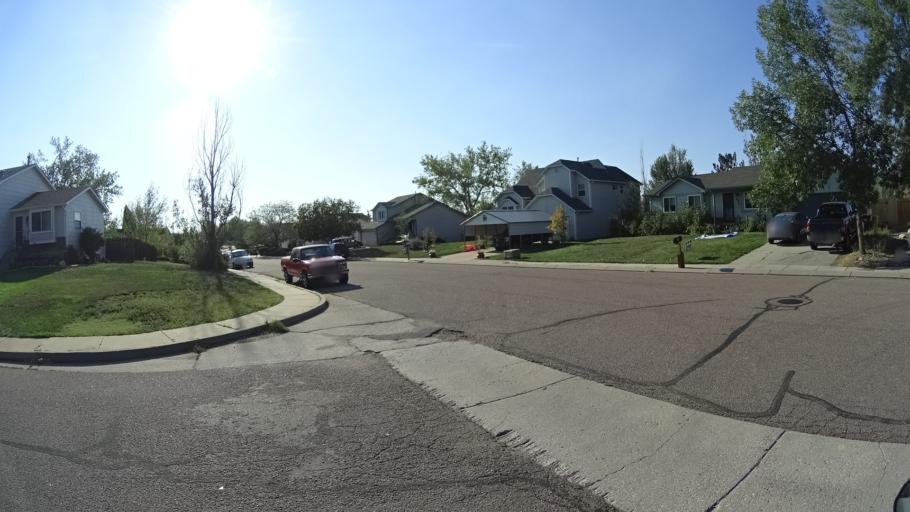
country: US
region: Colorado
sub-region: El Paso County
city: Stratmoor
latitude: 38.7741
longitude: -104.8033
